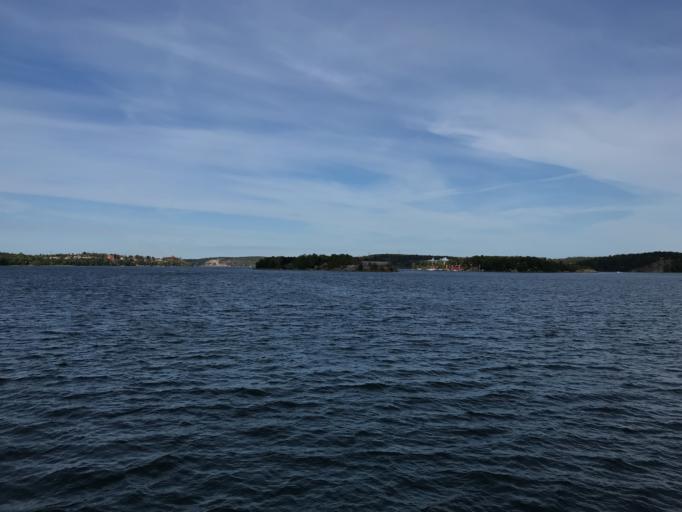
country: SE
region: Stockholm
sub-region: Nacka Kommun
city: Nacka
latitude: 59.3304
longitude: 18.1564
